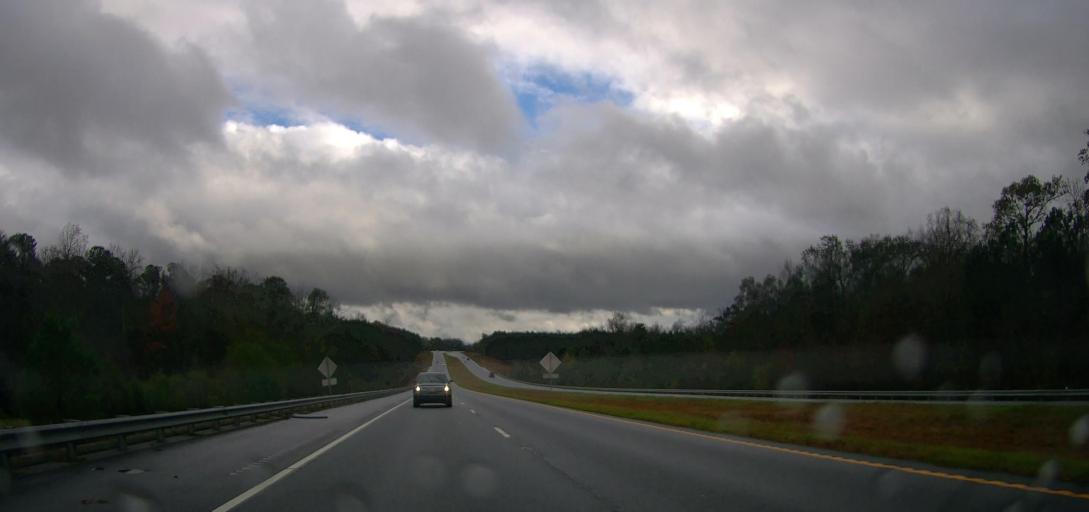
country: US
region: Georgia
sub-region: Jackson County
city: Nicholson
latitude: 34.0927
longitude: -83.4284
